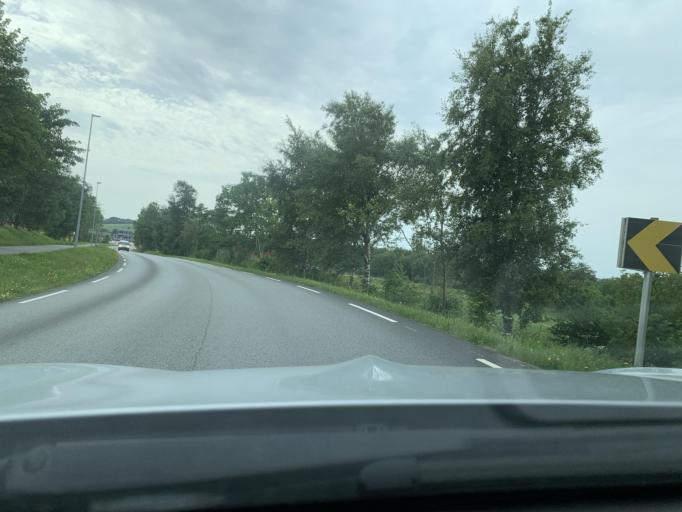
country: NO
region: Rogaland
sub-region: Time
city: Bryne
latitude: 58.7697
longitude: 5.7210
